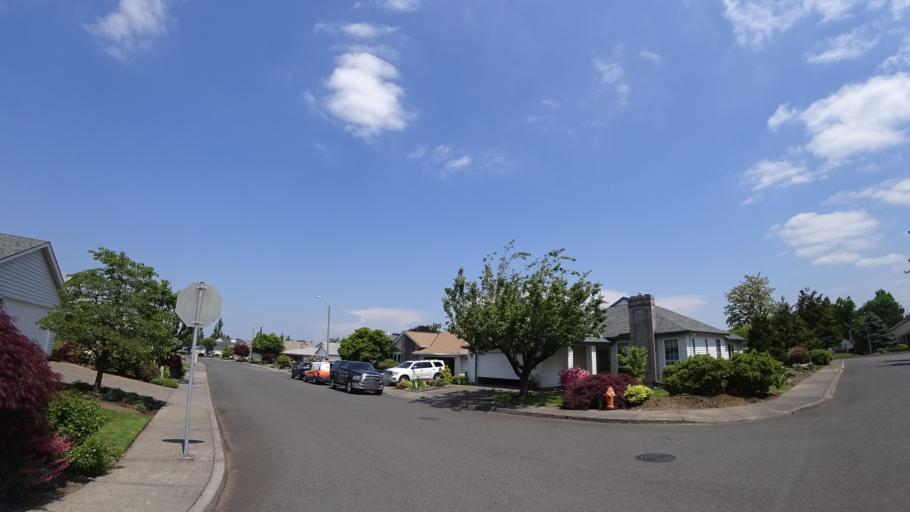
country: US
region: Oregon
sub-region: Multnomah County
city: Fairview
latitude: 45.5348
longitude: -122.5082
